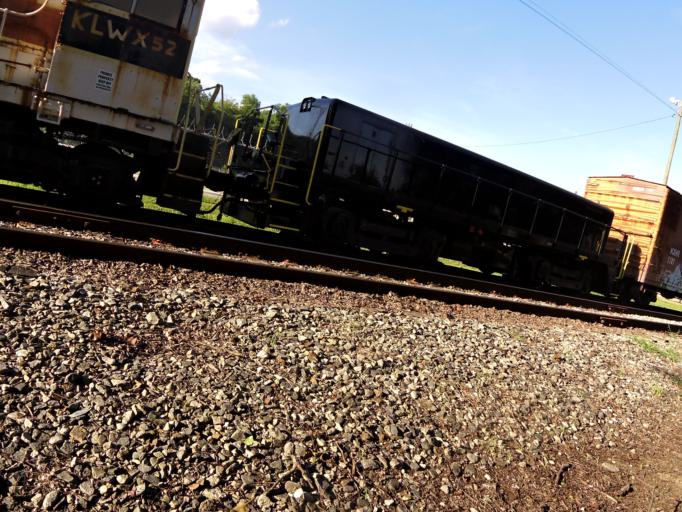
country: US
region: Tennessee
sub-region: Knox County
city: Knoxville
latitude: 35.9638
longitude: -83.8956
